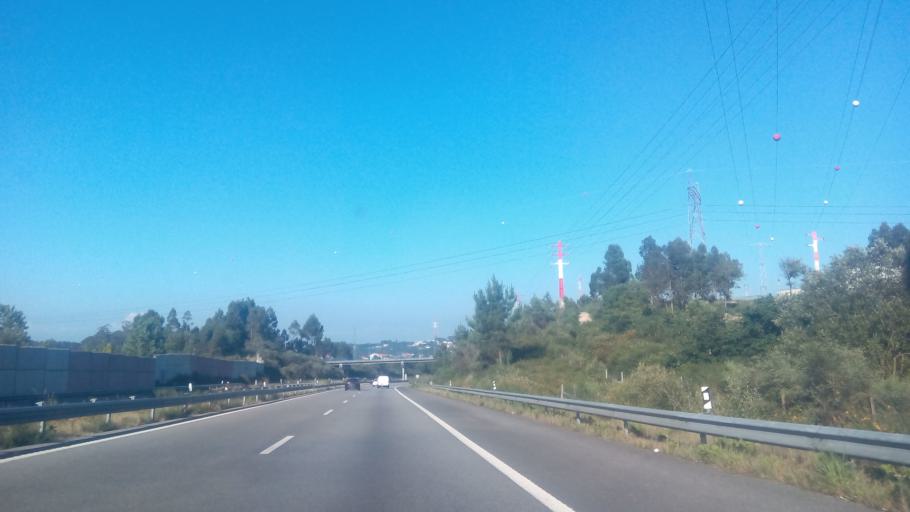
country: PT
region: Porto
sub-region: Pacos de Ferreira
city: Seroa
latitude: 41.2545
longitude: -8.4218
